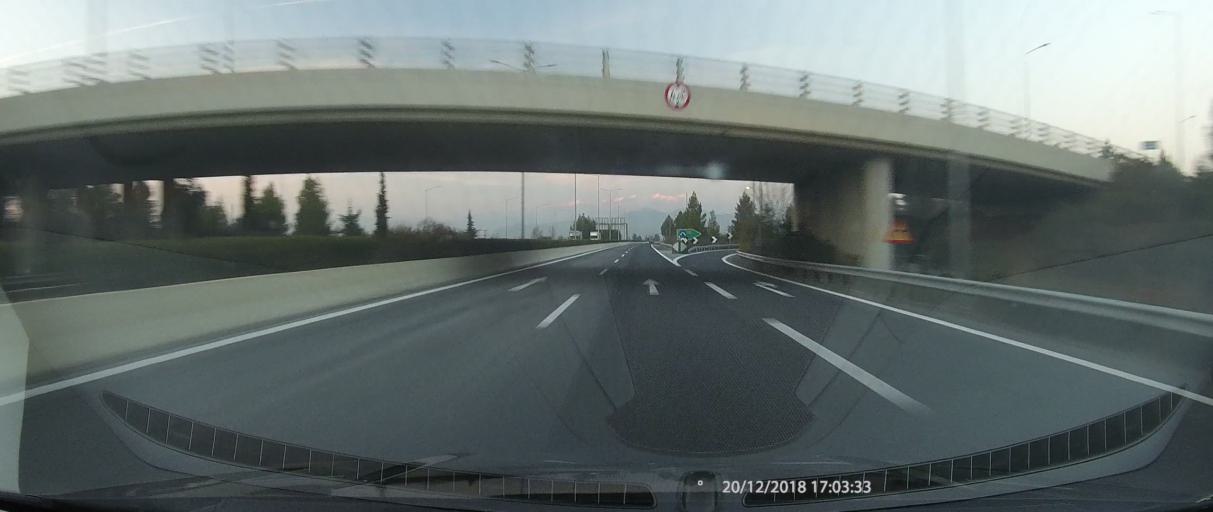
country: GR
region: Thessaly
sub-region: Nomos Larisis
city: Falani
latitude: 39.6989
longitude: 22.4875
